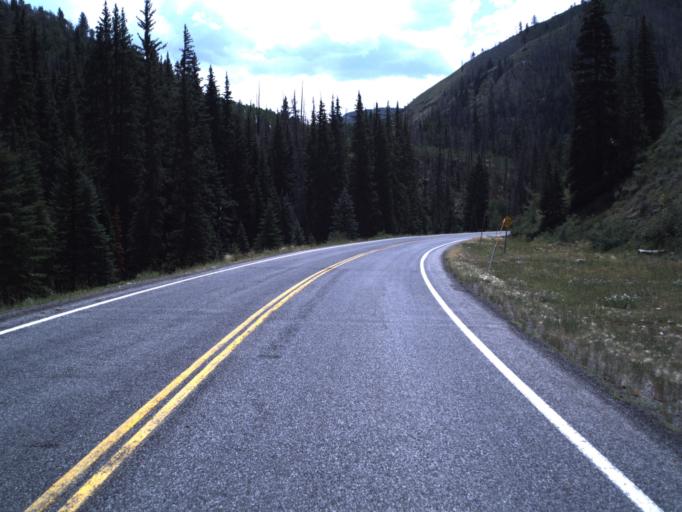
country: US
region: Utah
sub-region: Emery County
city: Huntington
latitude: 39.5056
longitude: -111.1563
